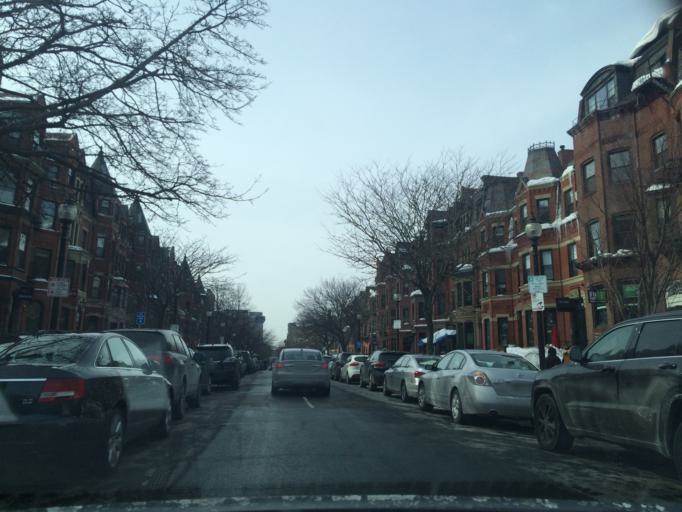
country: US
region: Massachusetts
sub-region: Suffolk County
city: Boston
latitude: 42.3497
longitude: -71.0822
